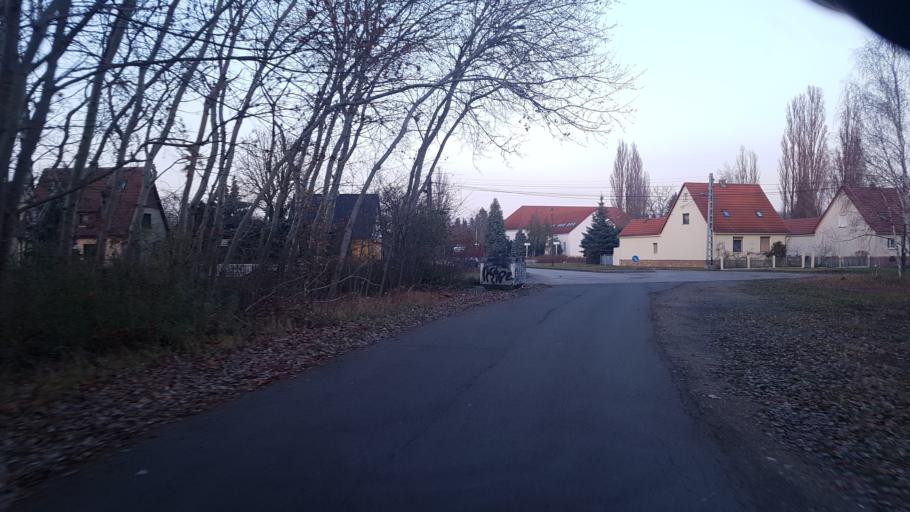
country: DE
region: Brandenburg
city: Lauchhammer
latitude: 51.4764
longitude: 13.7408
